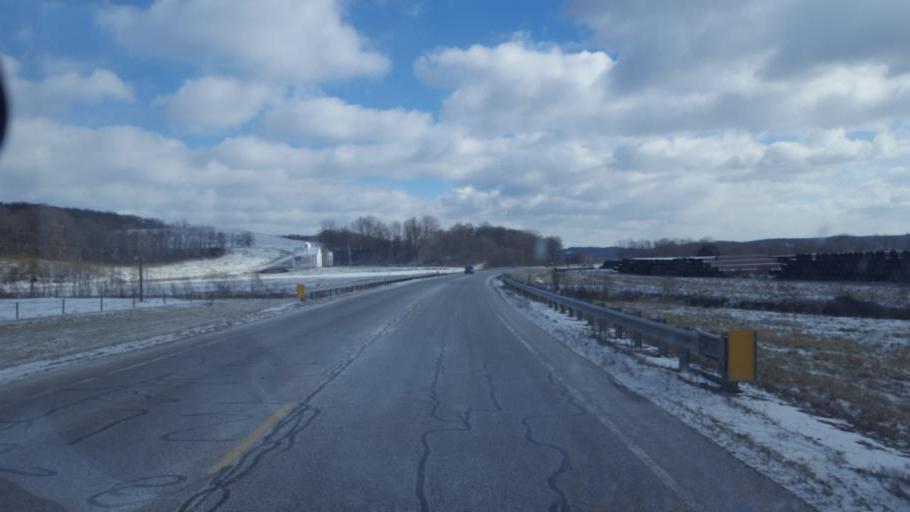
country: US
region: Ohio
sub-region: Muskingum County
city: Dresden
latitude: 40.1547
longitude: -81.9755
